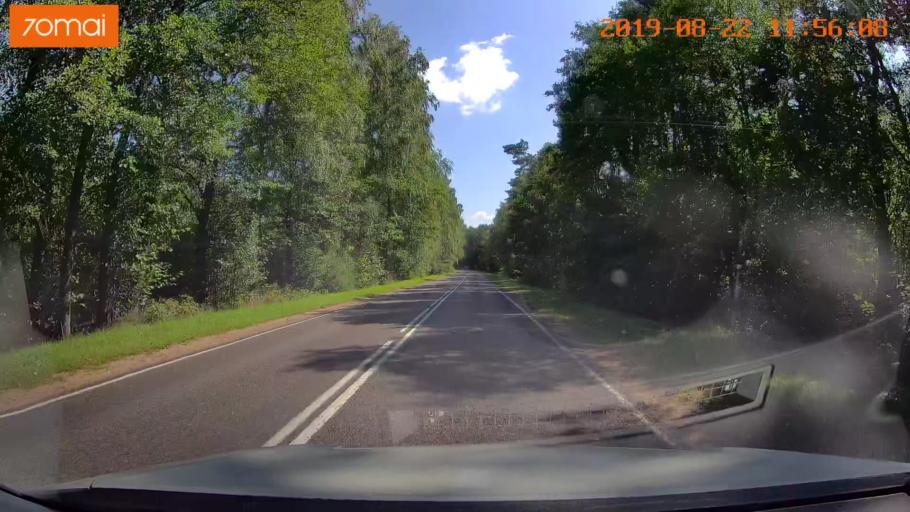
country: BY
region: Minsk
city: Prawdzinski
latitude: 53.4292
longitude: 27.5639
